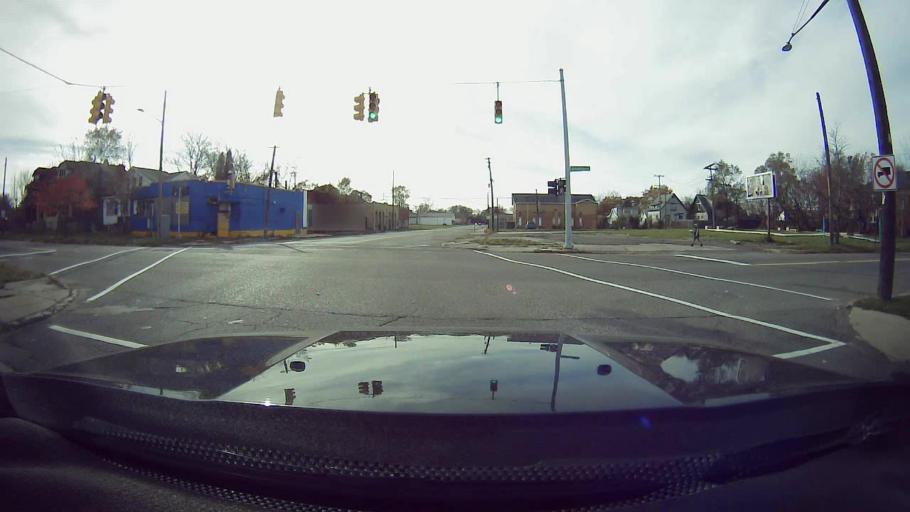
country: US
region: Michigan
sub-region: Wayne County
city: Highland Park
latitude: 42.3780
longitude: -83.1330
